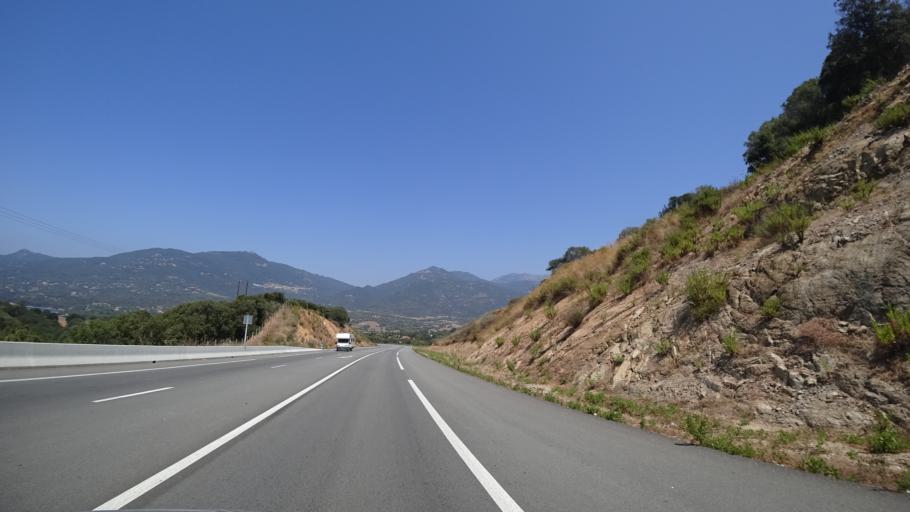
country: FR
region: Corsica
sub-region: Departement de la Corse-du-Sud
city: Propriano
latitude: 41.6767
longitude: 8.9280
